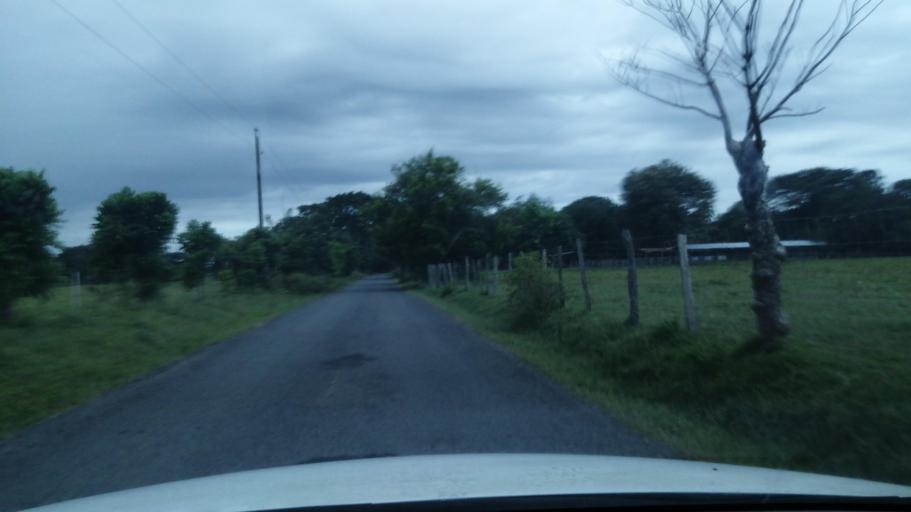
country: PA
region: Chiriqui
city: Alanje
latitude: 8.4034
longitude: -82.4997
